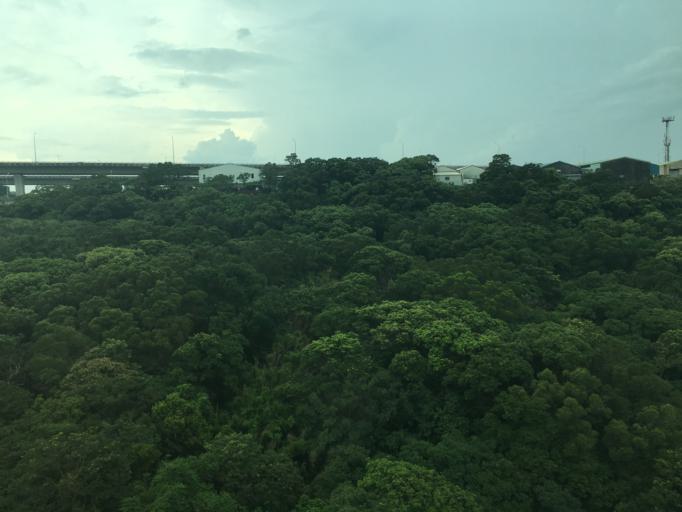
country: TW
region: Taiwan
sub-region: Taoyuan
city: Taoyuan
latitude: 25.0682
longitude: 121.3479
